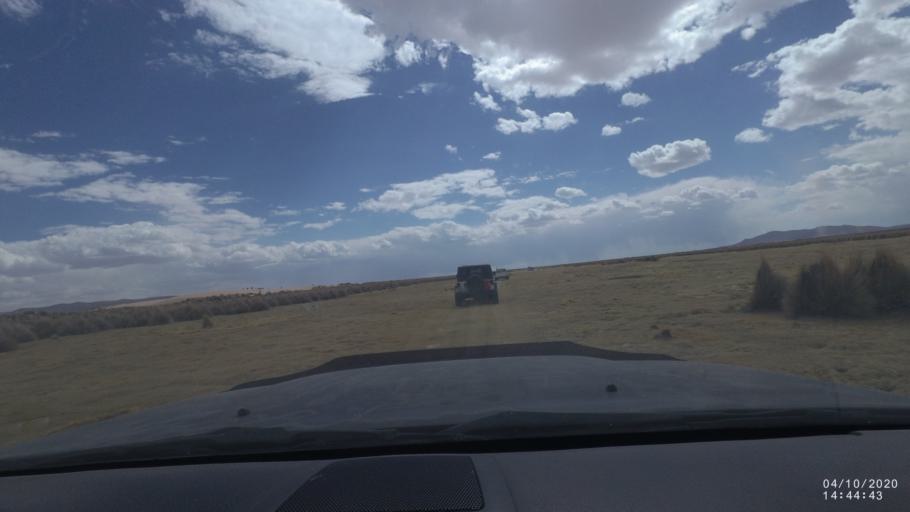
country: BO
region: Oruro
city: Poopo
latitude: -18.6869
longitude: -67.4963
